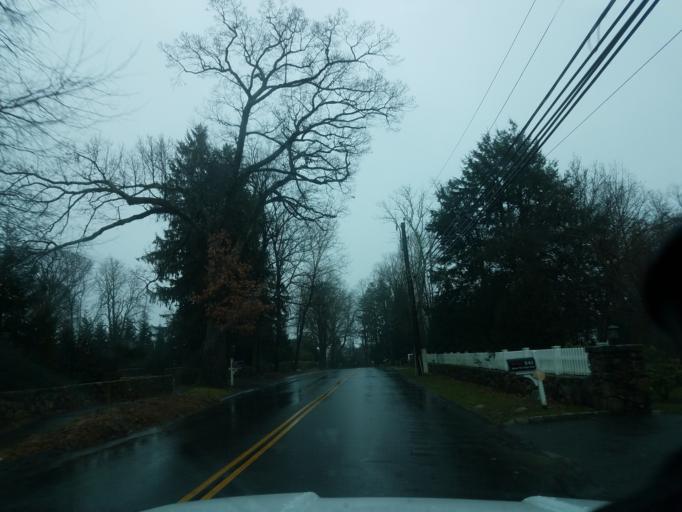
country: US
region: Connecticut
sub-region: Fairfield County
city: Darien
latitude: 41.0777
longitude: -73.4974
